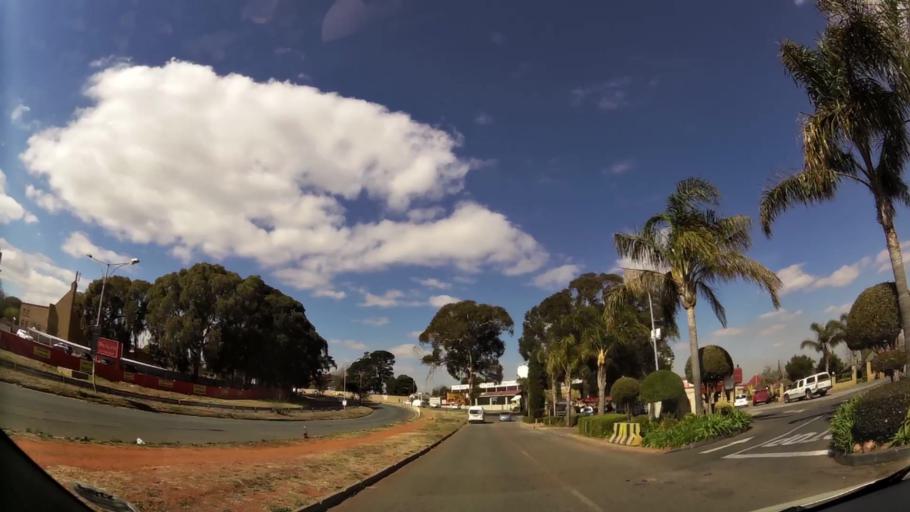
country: ZA
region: Gauteng
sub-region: West Rand District Municipality
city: Krugersdorp
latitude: -26.1116
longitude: 27.8051
